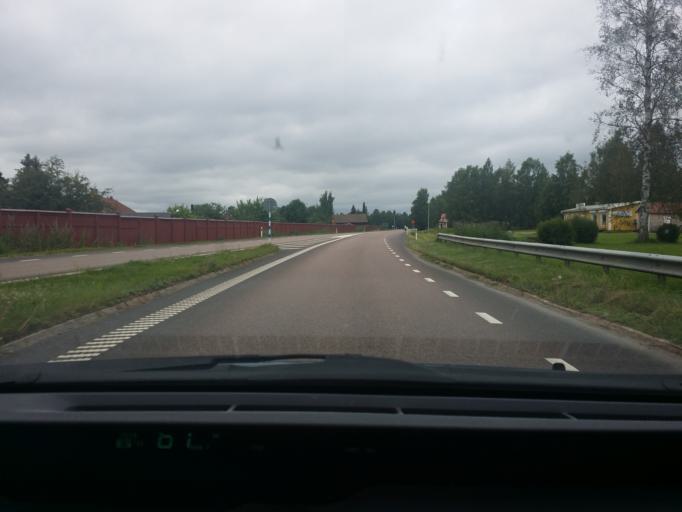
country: SE
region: Dalarna
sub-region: Gagnefs Kommun
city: Djuras
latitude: 60.5619
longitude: 15.1315
